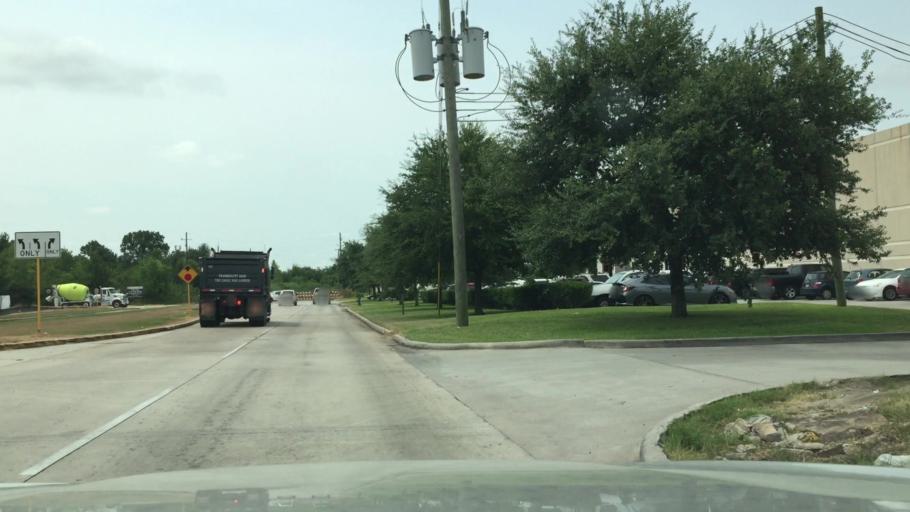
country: US
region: Texas
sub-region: Harris County
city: Jersey Village
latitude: 29.9284
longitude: -95.5438
